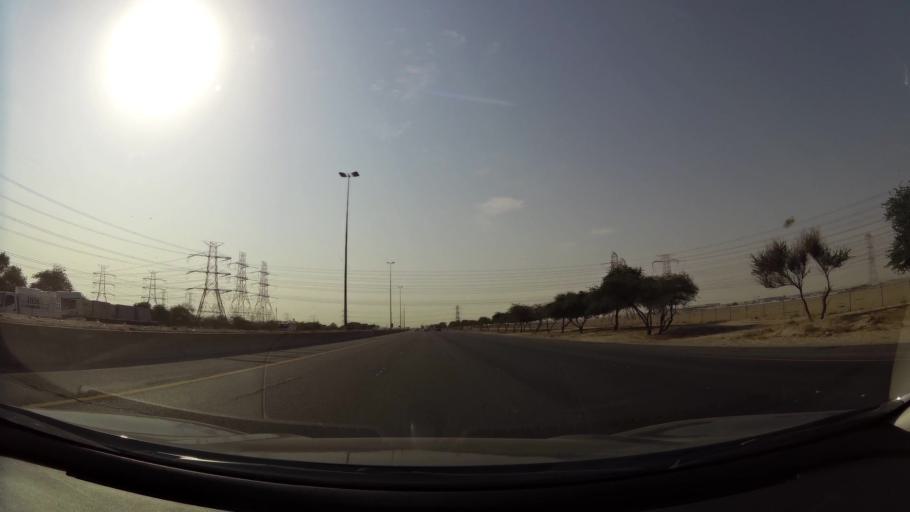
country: KW
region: Al Ahmadi
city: Al Ahmadi
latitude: 29.0142
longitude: 48.0927
